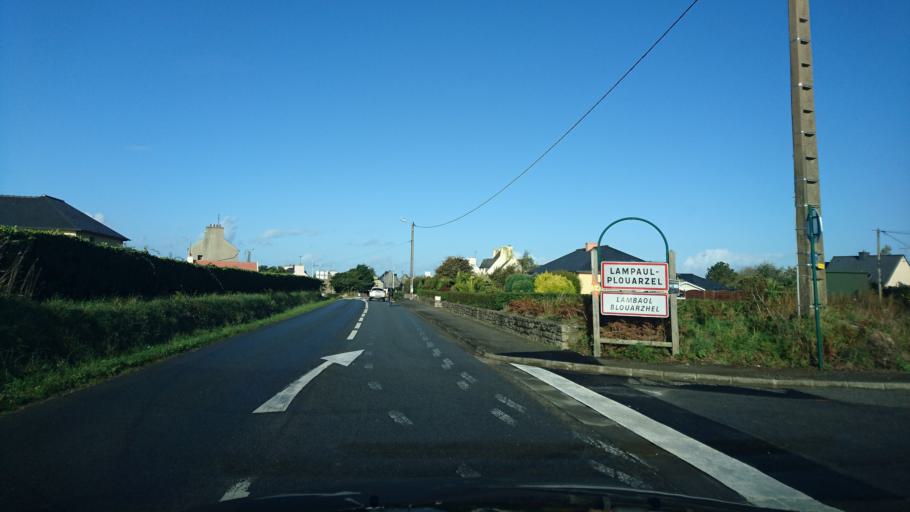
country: FR
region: Brittany
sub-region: Departement du Finistere
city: Lampaul-Plouarzel
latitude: 48.4448
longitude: -4.7527
